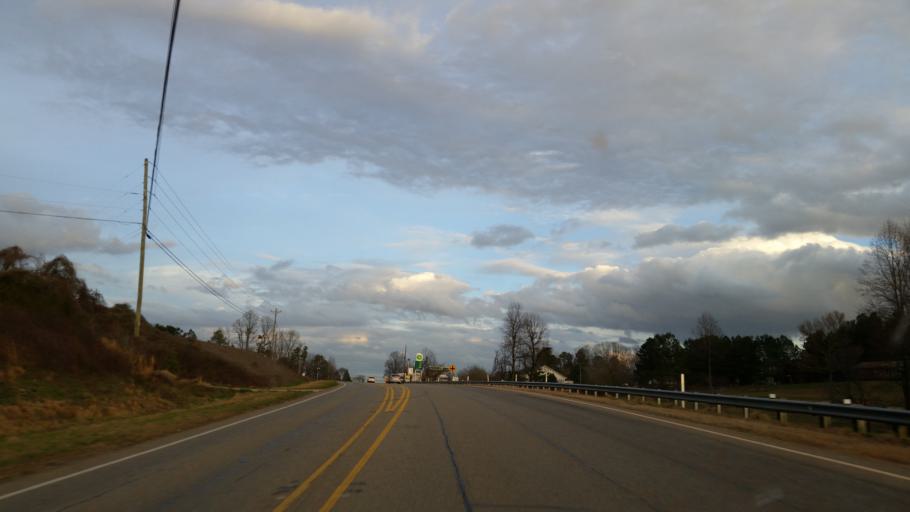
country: US
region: Georgia
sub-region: Pickens County
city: Jasper
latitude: 34.4699
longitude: -84.5123
